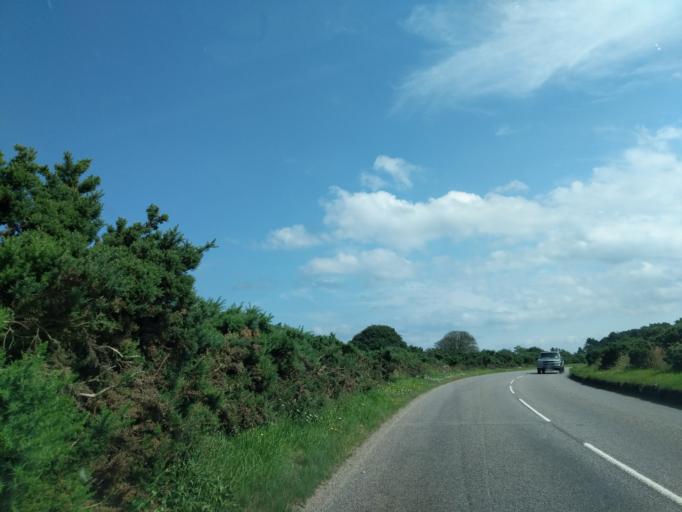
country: GB
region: Scotland
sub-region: Moray
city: Lossiemouth
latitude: 57.7168
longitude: -3.3142
